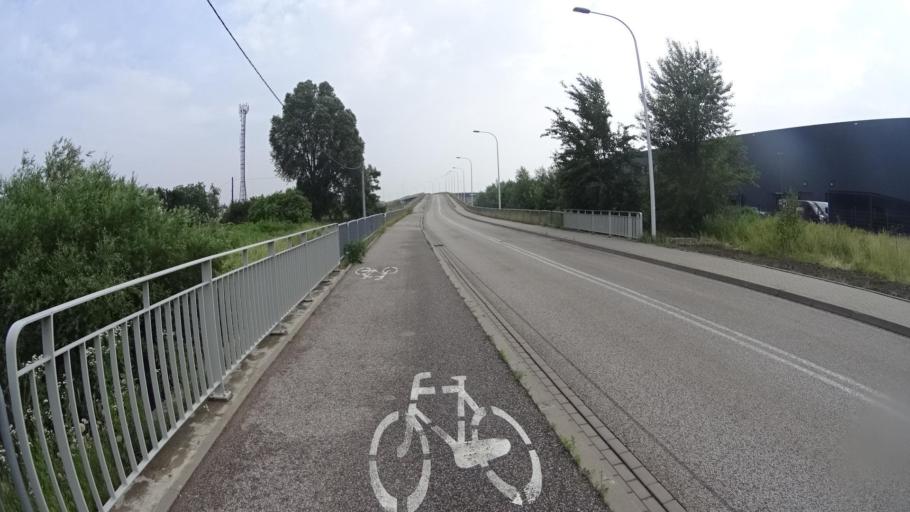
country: PL
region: Masovian Voivodeship
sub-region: Powiat pruszkowski
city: Nowe Grocholice
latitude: 52.1743
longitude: 20.9193
